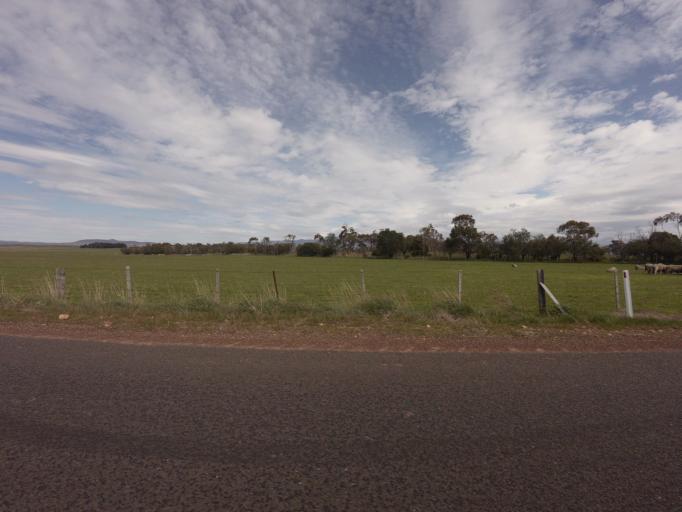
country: AU
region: Tasmania
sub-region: Northern Midlands
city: Evandale
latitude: -41.7986
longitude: 147.2565
